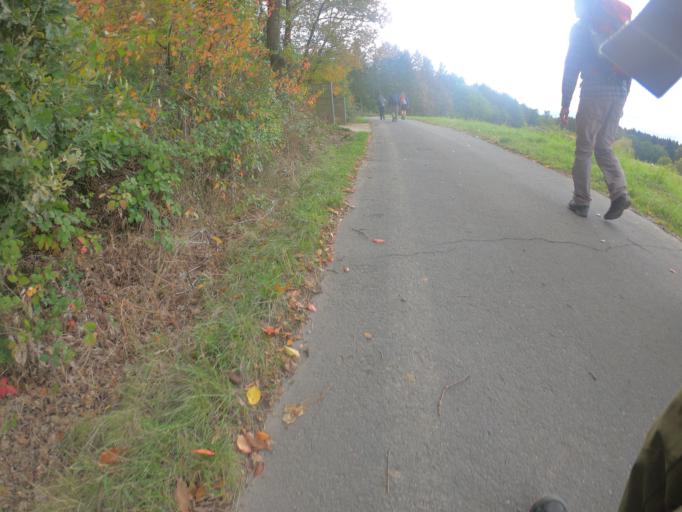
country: DE
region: Hesse
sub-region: Regierungsbezirk Darmstadt
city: Niedernhausen
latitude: 50.1924
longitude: 8.3176
